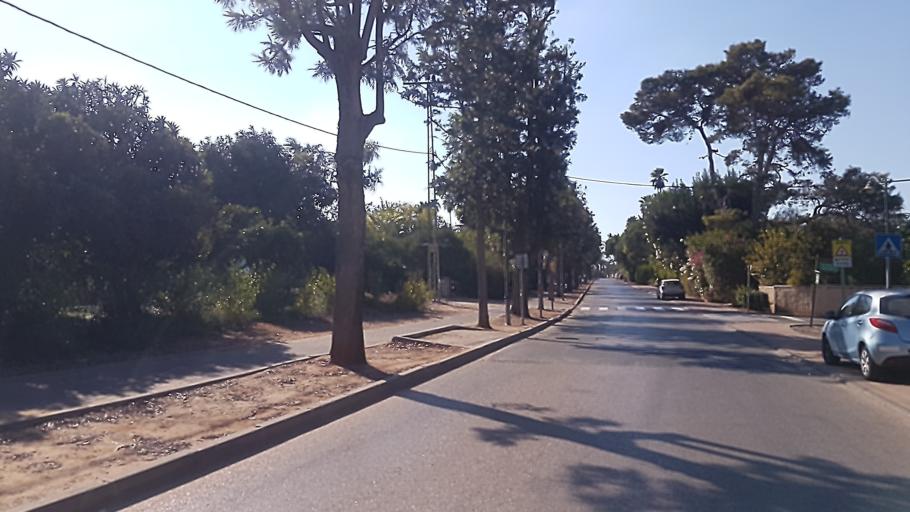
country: IL
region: Central District
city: Ra'anana
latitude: 32.2110
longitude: 34.8968
